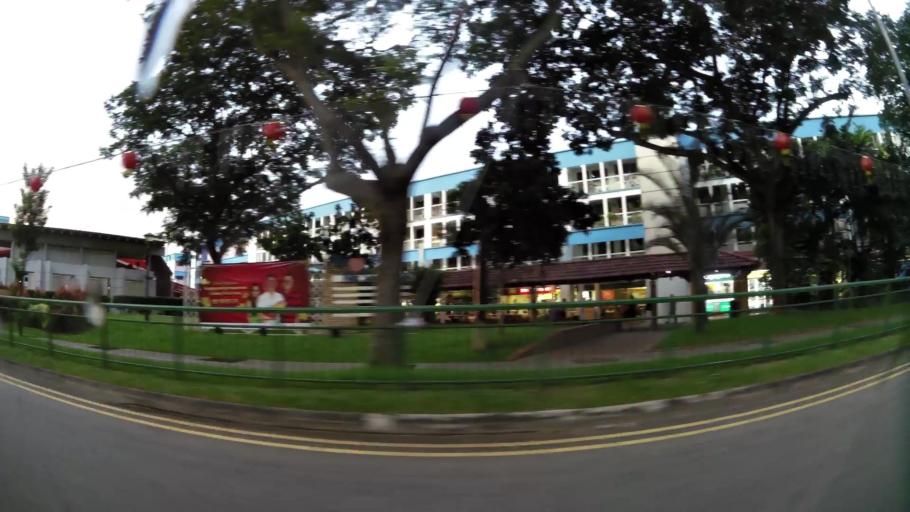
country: MY
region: Johor
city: Kampung Pasir Gudang Baru
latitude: 1.4357
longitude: 103.8377
